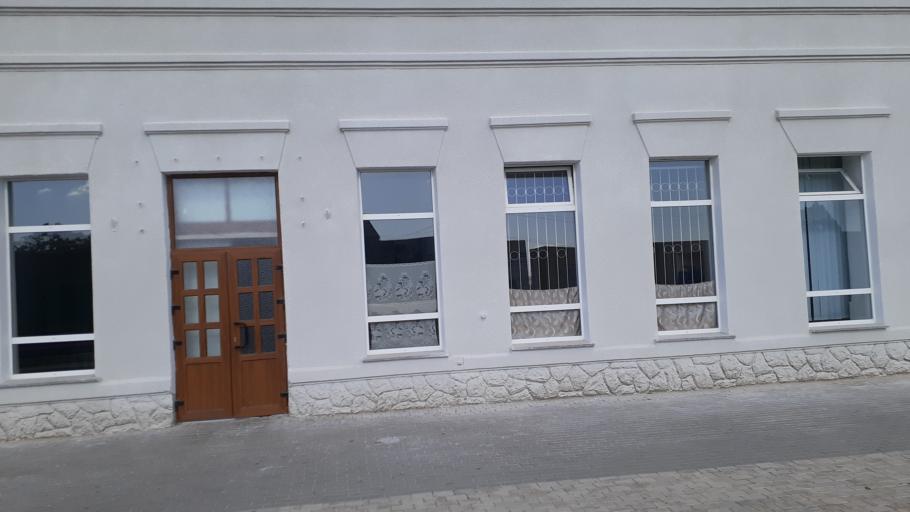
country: MD
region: Drochia
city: Drochia
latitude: 48.0309
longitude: 27.8098
